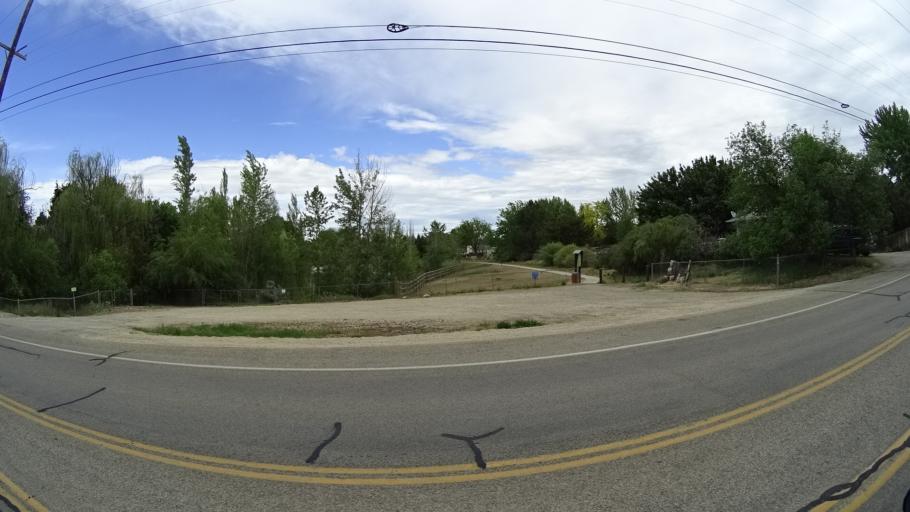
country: US
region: Idaho
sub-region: Ada County
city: Meridian
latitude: 43.5757
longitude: -116.3171
